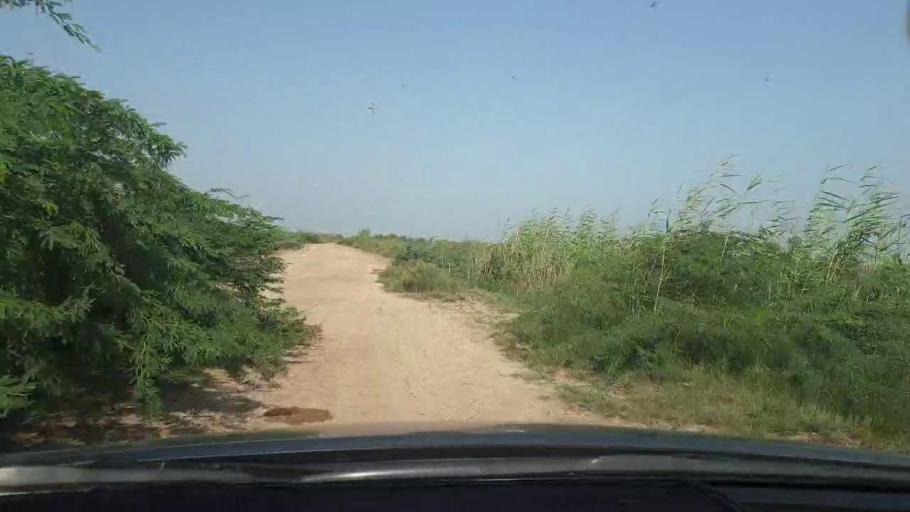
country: PK
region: Sindh
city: Tando Bago
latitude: 24.7095
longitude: 69.1102
